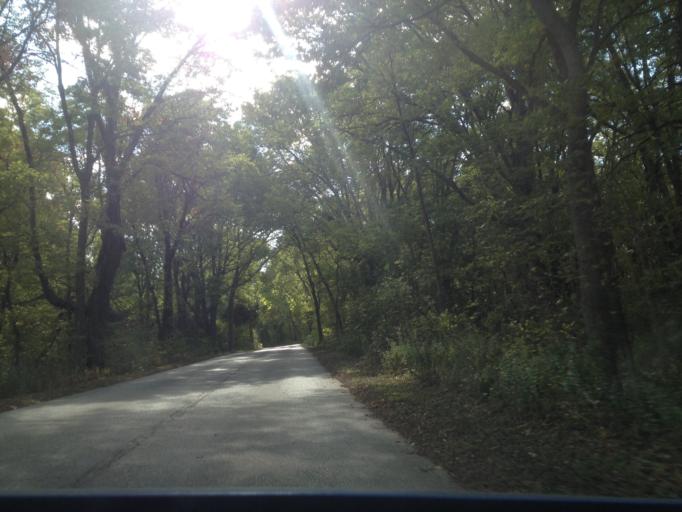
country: CA
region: Ontario
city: Amherstburg
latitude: 41.9714
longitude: -82.5347
